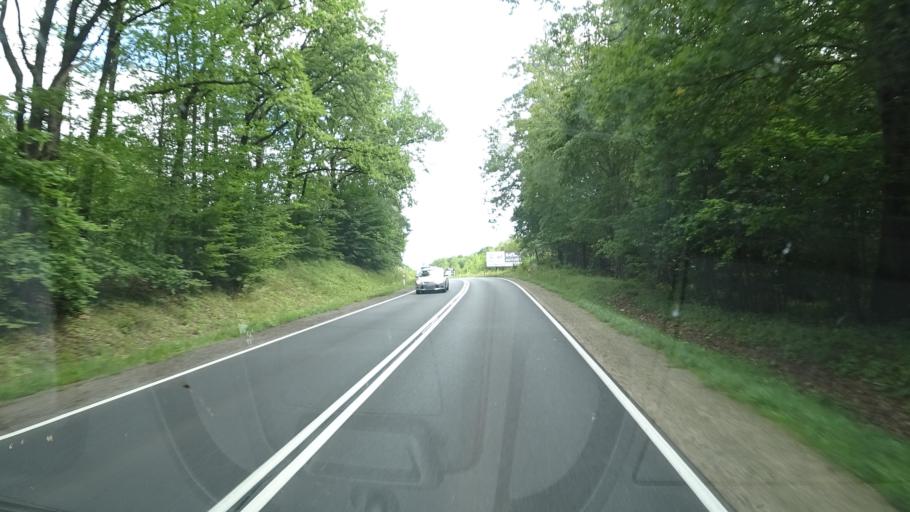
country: PL
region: Warmian-Masurian Voivodeship
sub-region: Powiat elcki
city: Elk
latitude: 53.8277
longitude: 22.3091
